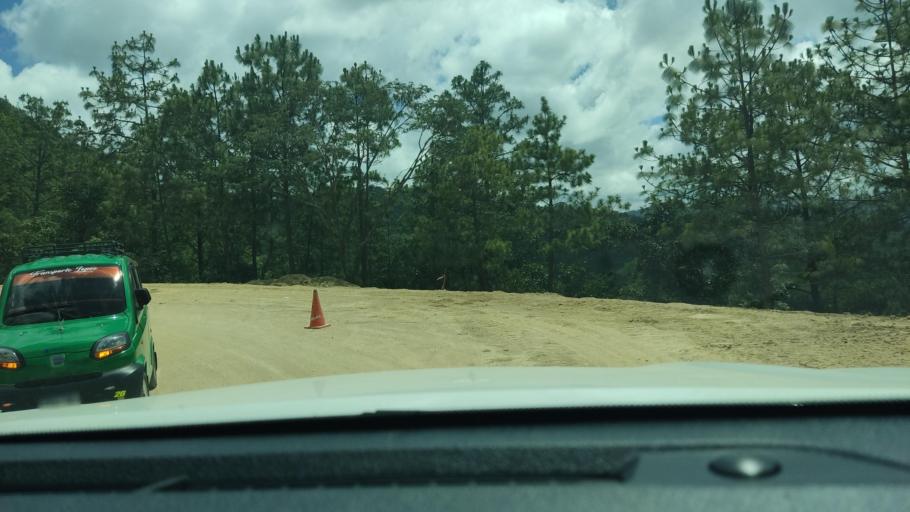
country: GT
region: Chimaltenango
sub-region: Municipio de San Juan Comalapa
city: Comalapa
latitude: 14.7875
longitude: -90.8638
